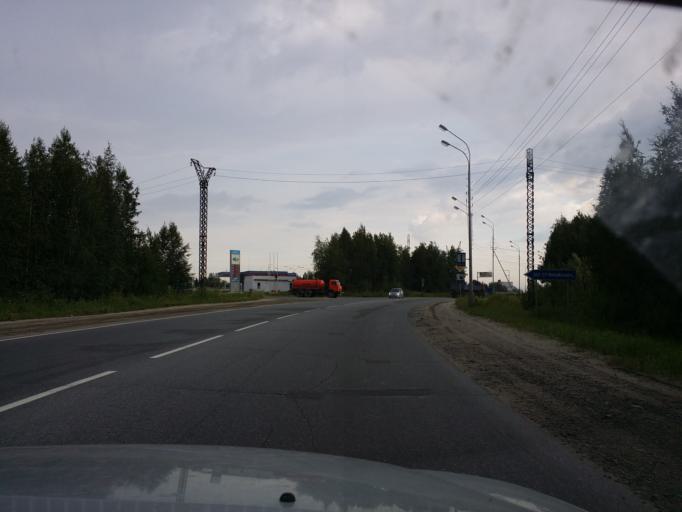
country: RU
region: Khanty-Mansiyskiy Avtonomnyy Okrug
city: Megion
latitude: 61.0490
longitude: 76.1122
